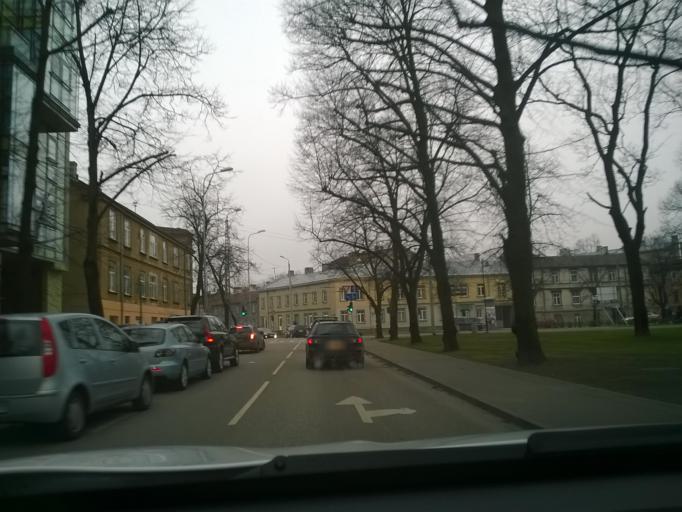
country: LV
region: Riga
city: Riga
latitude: 56.9566
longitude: 24.1541
